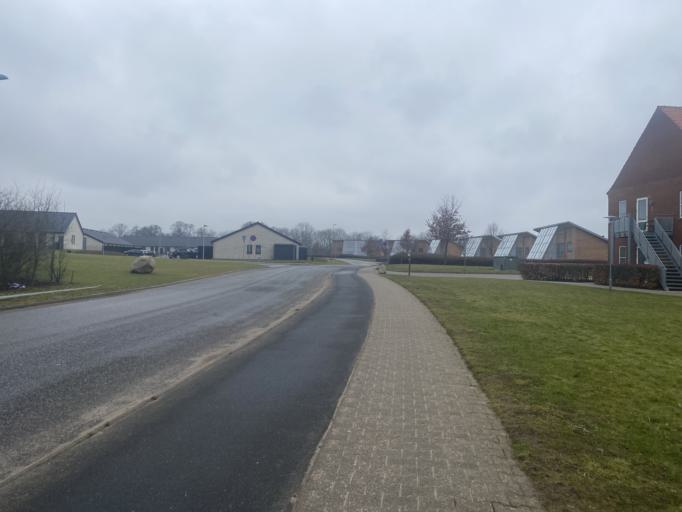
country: DK
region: South Denmark
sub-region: Fredericia Kommune
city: Fredericia
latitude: 55.5705
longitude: 9.7029
